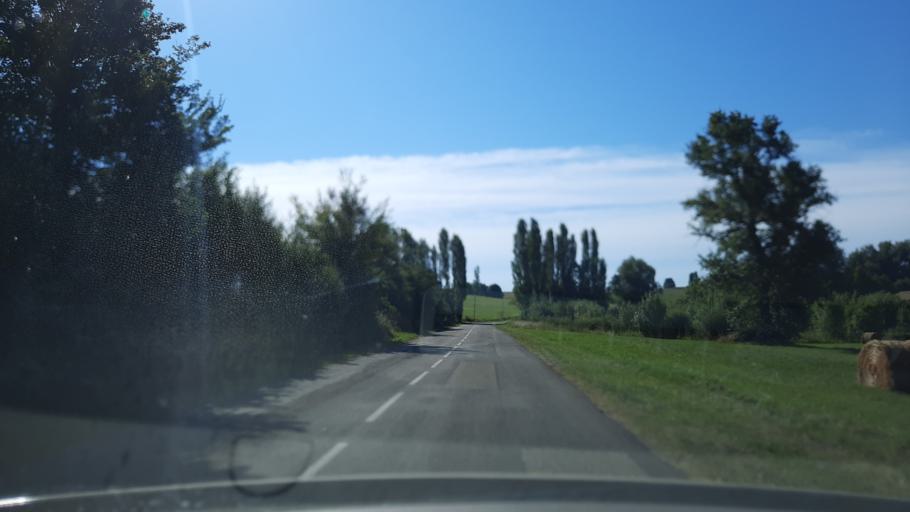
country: FR
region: Midi-Pyrenees
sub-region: Departement du Tarn-et-Garonne
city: Molieres
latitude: 44.1979
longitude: 1.4309
